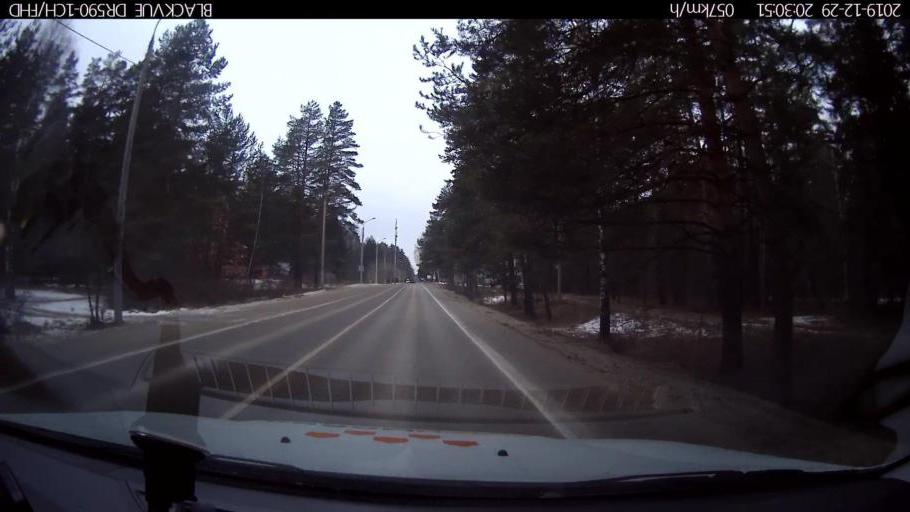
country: RU
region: Nizjnij Novgorod
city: Afonino
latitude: 56.1750
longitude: 44.0881
